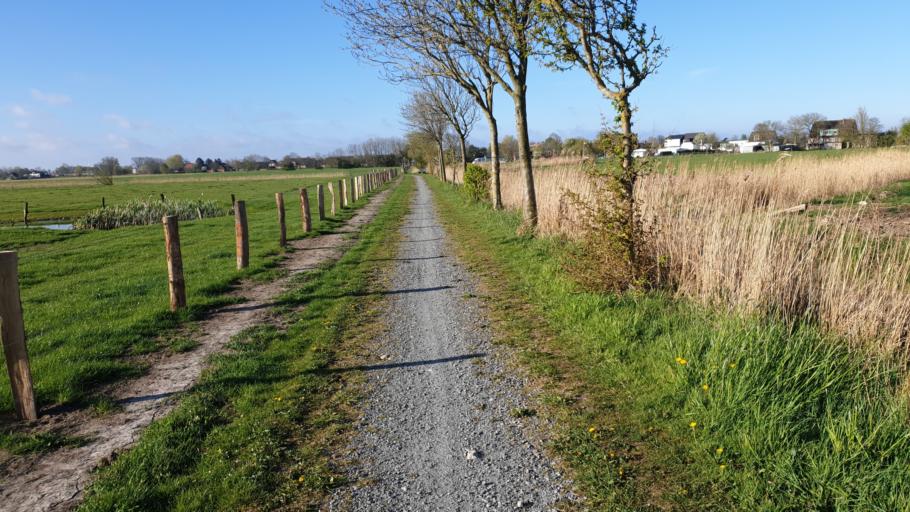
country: DE
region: Schleswig-Holstein
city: Elisabeth-Sophien-Koog
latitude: 54.4907
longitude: 8.8629
